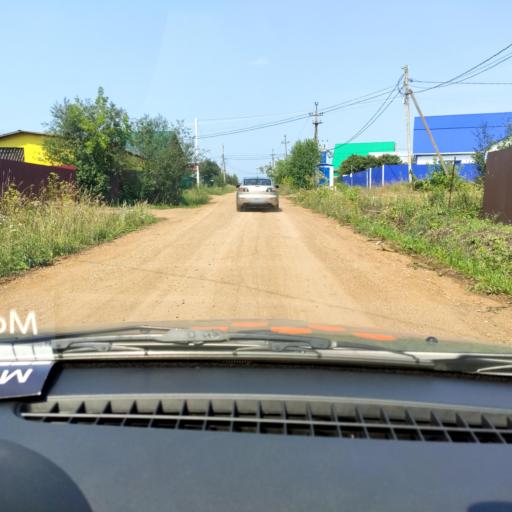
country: RU
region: Bashkortostan
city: Iglino
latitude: 54.8409
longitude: 56.3997
